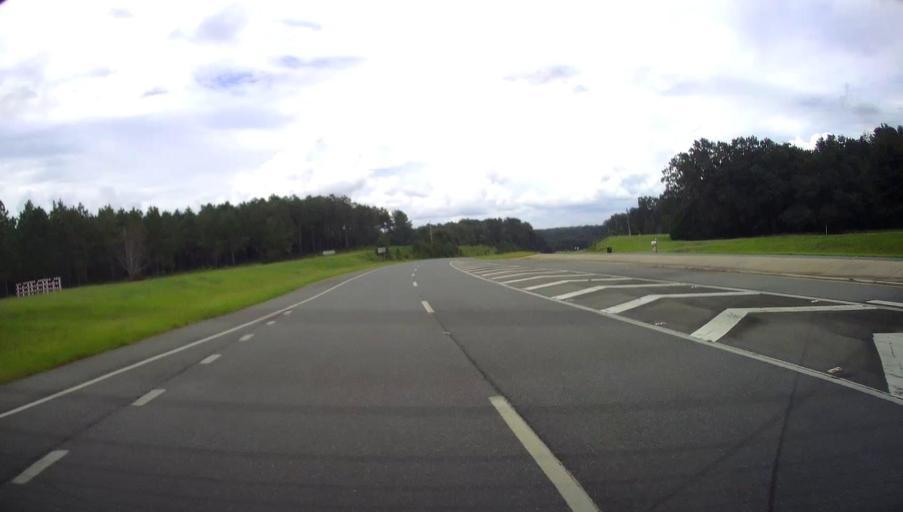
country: US
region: Georgia
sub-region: Schley County
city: Ellaville
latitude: 32.2564
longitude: -84.3038
